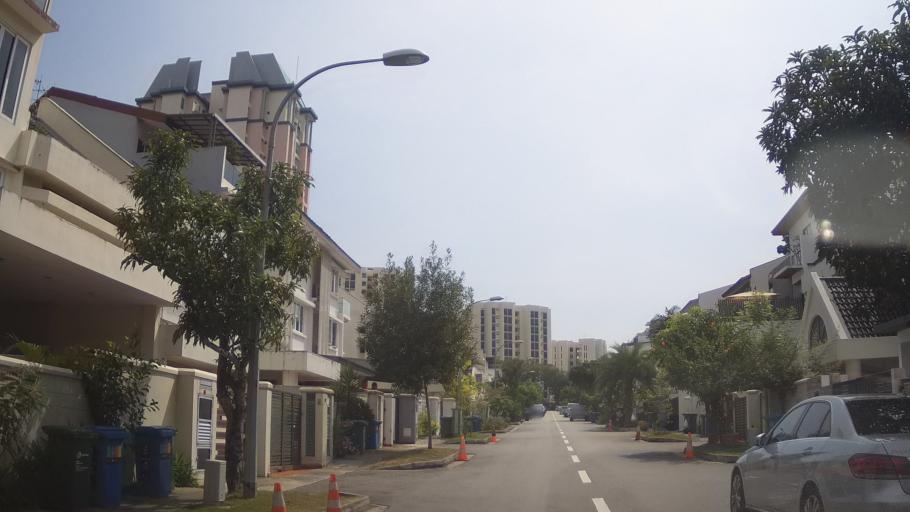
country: MY
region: Johor
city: Johor Bahru
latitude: 1.3716
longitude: 103.7641
